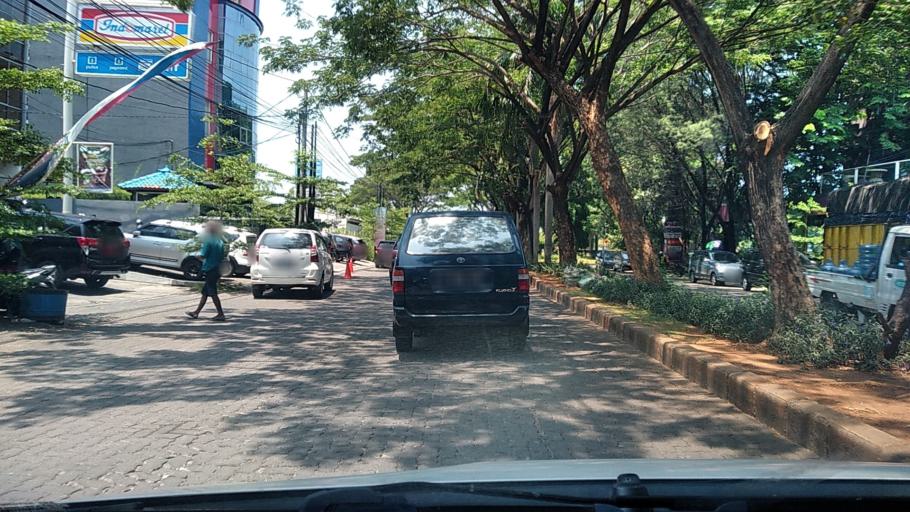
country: ID
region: Central Java
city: Semarang
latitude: -6.9638
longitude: 110.3906
